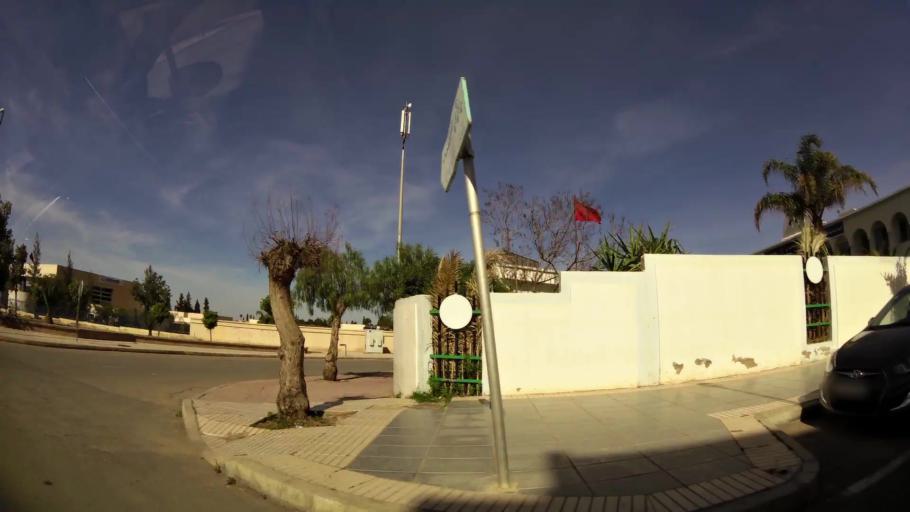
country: MA
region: Oriental
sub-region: Oujda-Angad
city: Oujda
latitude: 34.6707
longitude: -1.9119
